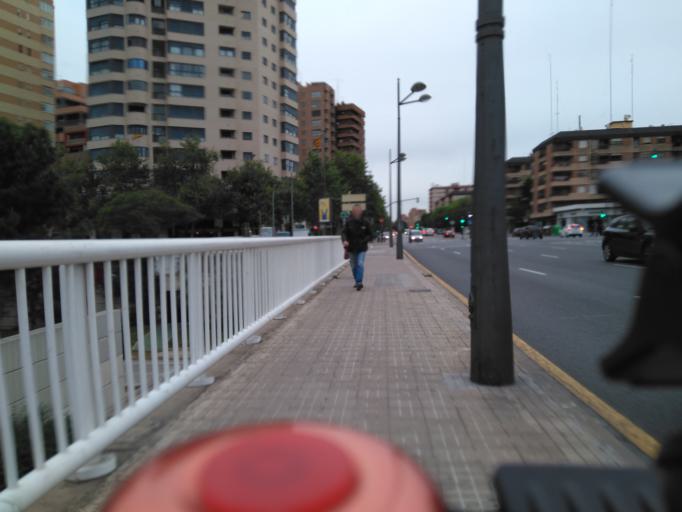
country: ES
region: Valencia
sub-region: Provincia de Valencia
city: Valencia
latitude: 39.4758
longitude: -0.3968
